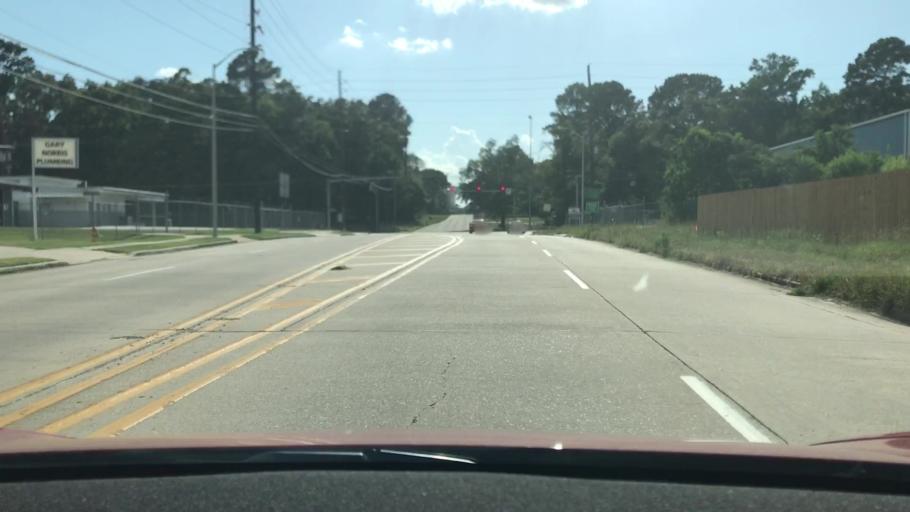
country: US
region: Louisiana
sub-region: Bossier Parish
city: Bossier City
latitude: 32.4130
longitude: -93.7792
